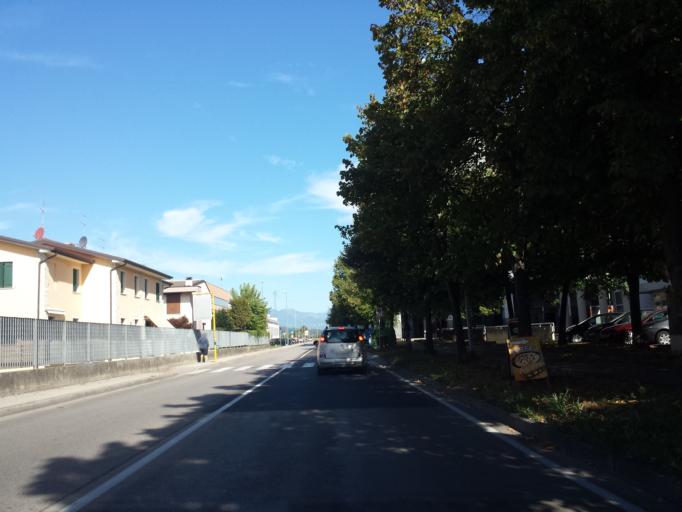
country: IT
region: Veneto
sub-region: Provincia di Vicenza
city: Creazzo
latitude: 45.5383
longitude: 11.5113
